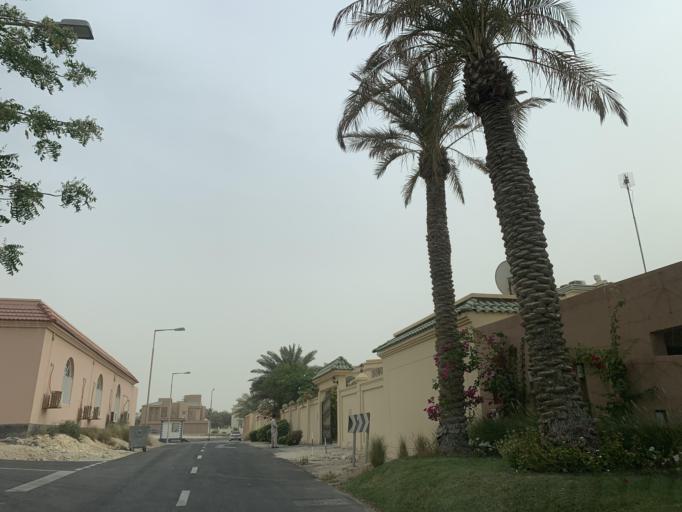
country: BH
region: Central Governorate
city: Madinat Hamad
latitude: 26.1404
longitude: 50.5218
